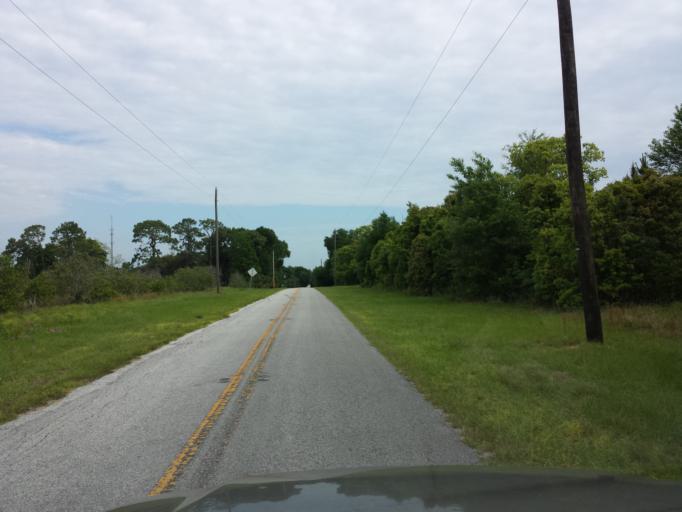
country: US
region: Florida
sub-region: Pasco County
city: San Antonio
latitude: 28.4152
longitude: -82.2783
